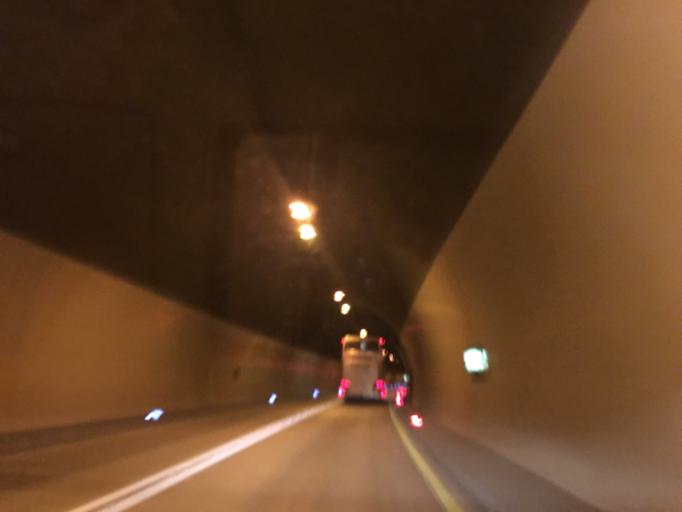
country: ME
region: Bar
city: Sutomore
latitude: 42.2269
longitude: 19.0534
